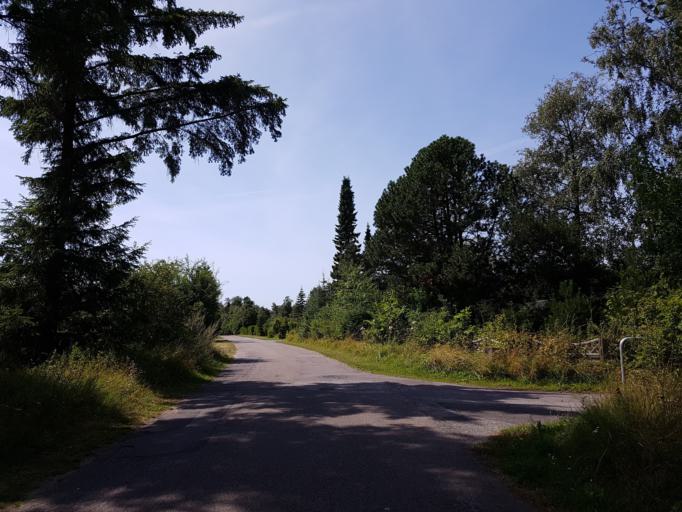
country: DK
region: Zealand
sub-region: Guldborgsund Kommune
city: Nykobing Falster
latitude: 54.6062
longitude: 11.9554
